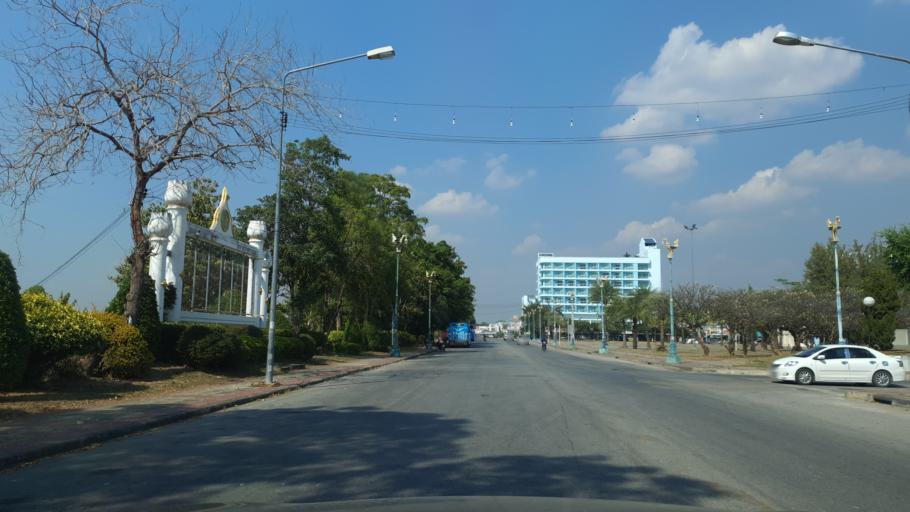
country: TH
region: Tak
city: Tak
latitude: 16.8695
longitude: 99.1235
